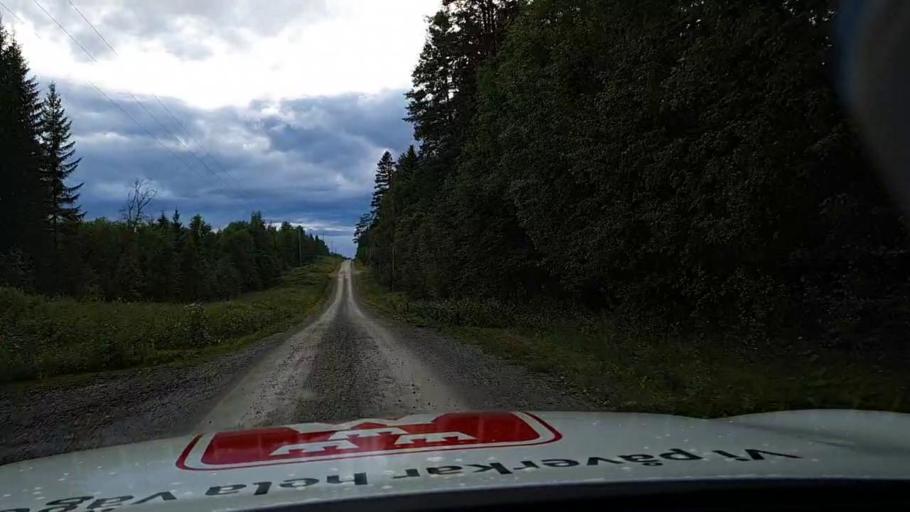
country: SE
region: Jaemtland
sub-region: Bergs Kommun
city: Hoverberg
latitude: 62.8846
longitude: 14.5856
